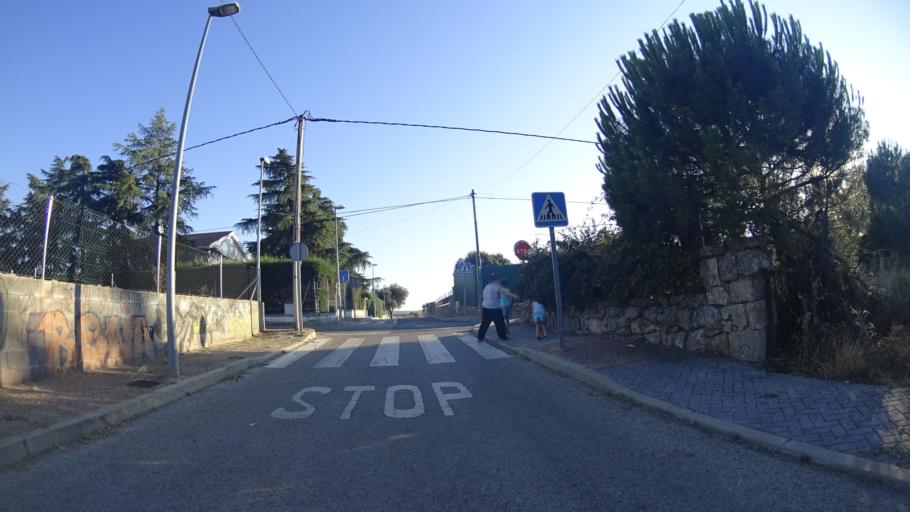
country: ES
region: Madrid
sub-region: Provincia de Madrid
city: Galapagar
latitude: 40.5676
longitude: -4.0027
